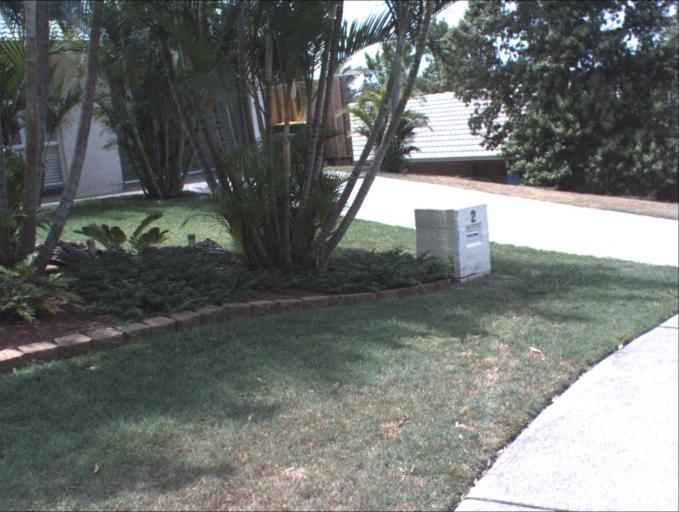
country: AU
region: Queensland
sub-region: Logan
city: Slacks Creek
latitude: -27.6585
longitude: 153.1970
